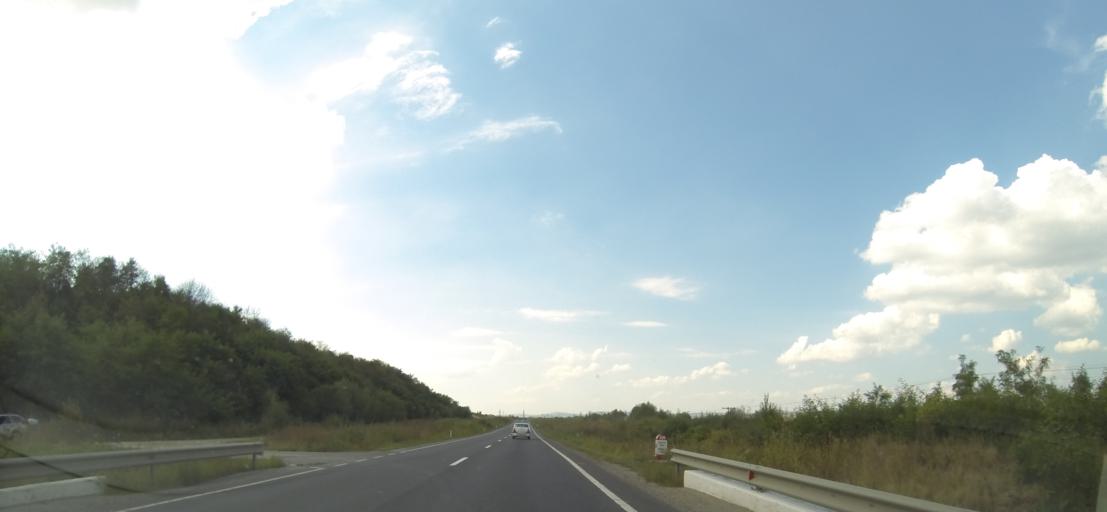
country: RO
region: Brasov
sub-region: Comuna Mandra
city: Mandra
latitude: 45.8223
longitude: 25.0674
